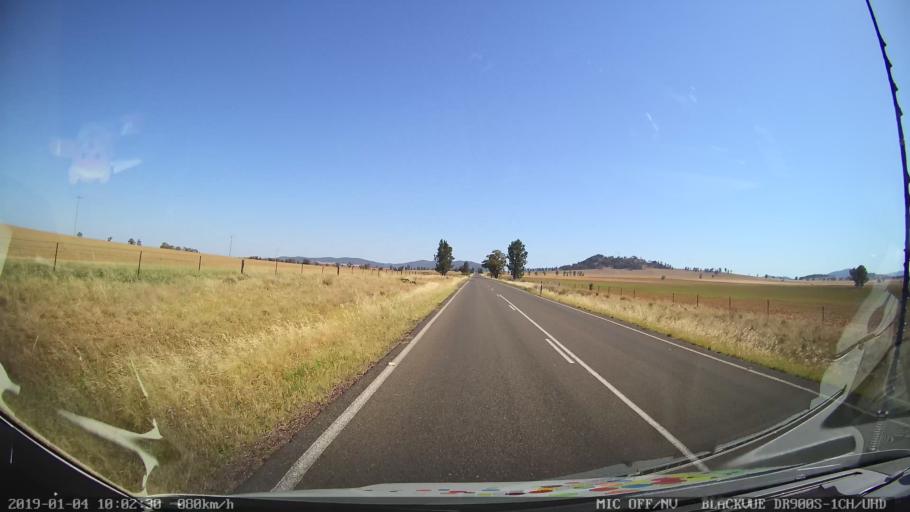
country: AU
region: New South Wales
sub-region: Cabonne
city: Canowindra
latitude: -33.4755
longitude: 148.3654
